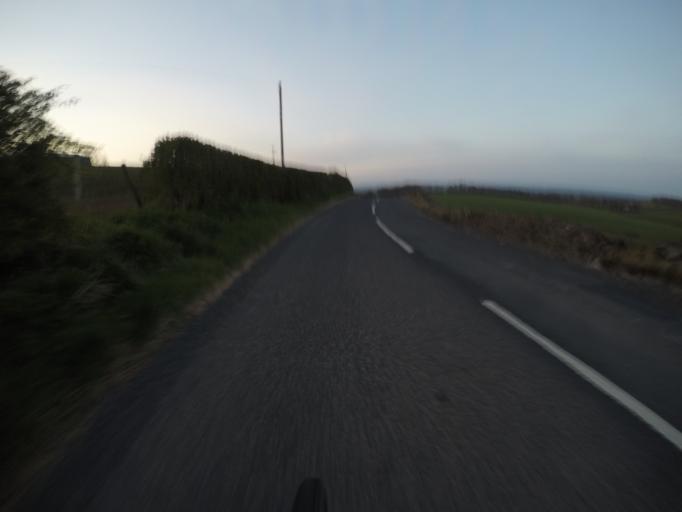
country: GB
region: Scotland
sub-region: South Ayrshire
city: Dundonald
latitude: 55.5657
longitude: -4.6017
